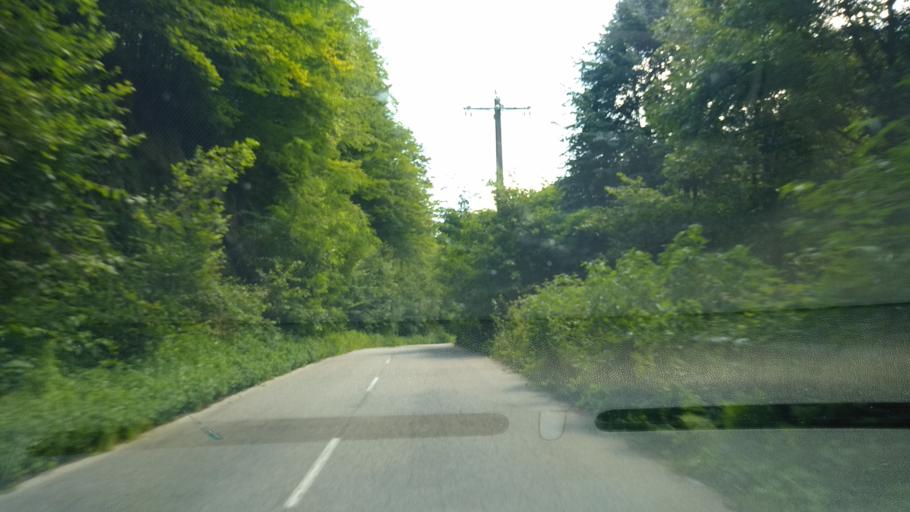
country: RO
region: Hunedoara
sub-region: Comuna Orastioara de Sus
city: Orastioara de Sus
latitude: 45.6655
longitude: 23.1717
